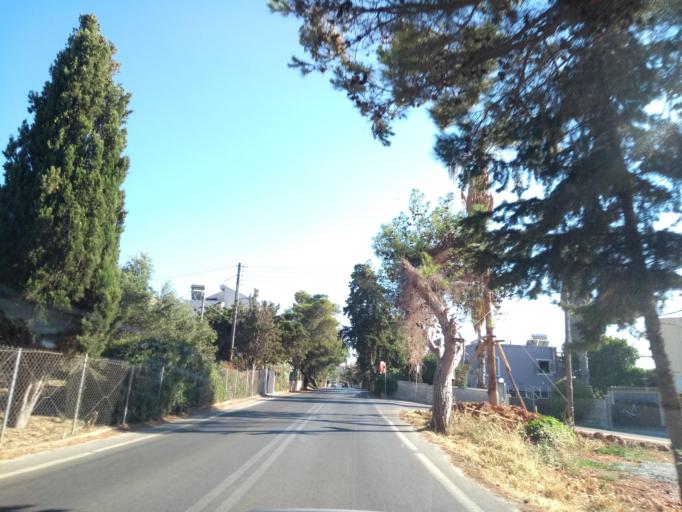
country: GR
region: Crete
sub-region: Nomos Chanias
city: Pithari
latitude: 35.5497
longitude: 24.0842
